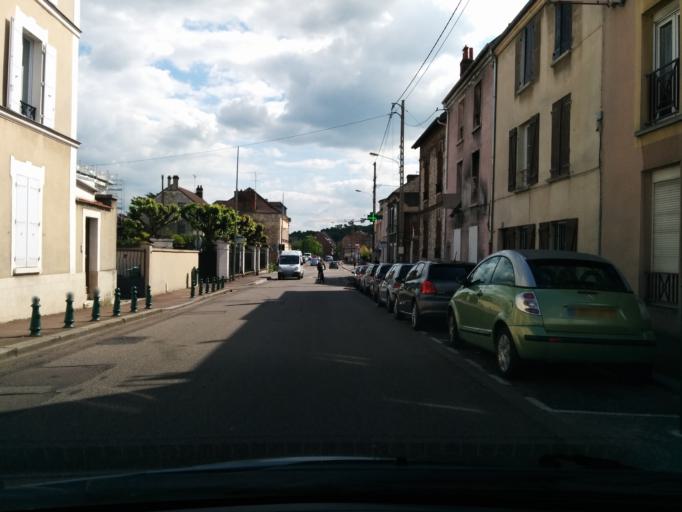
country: FR
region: Ile-de-France
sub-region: Departement des Yvelines
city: Mantes-la-Jolie
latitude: 48.9787
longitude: 1.7147
